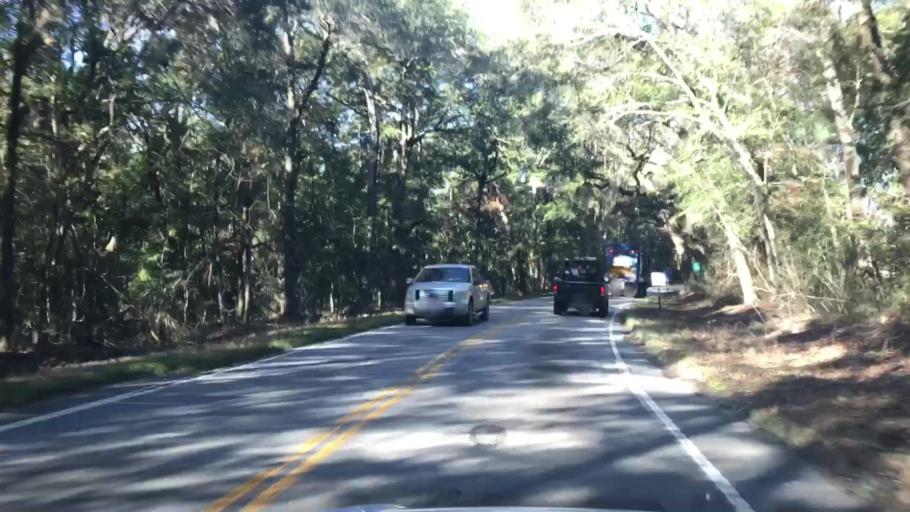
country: US
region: South Carolina
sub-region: Berkeley County
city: Ladson
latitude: 32.8902
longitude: -80.1279
